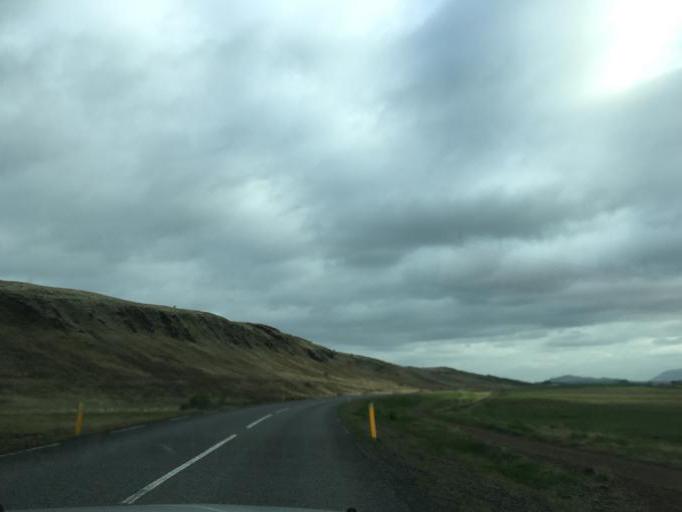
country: IS
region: South
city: Vestmannaeyjar
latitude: 64.1723
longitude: -20.2849
